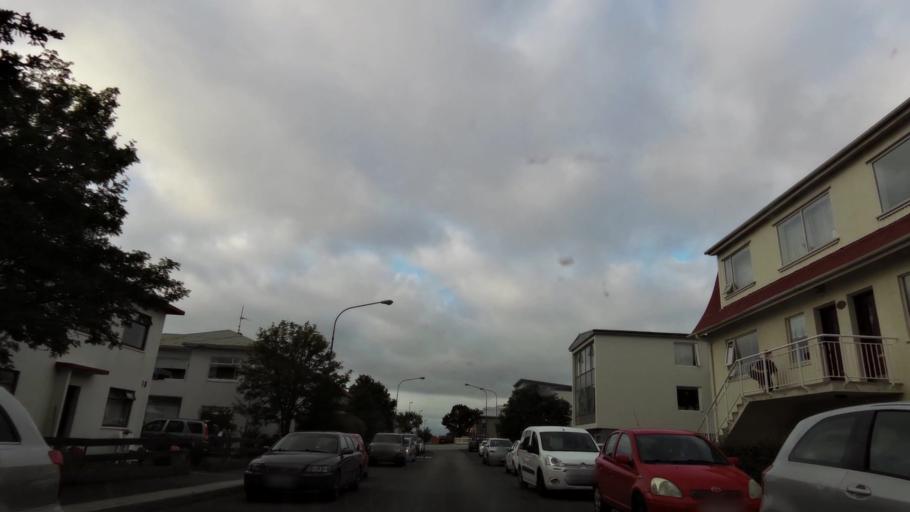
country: IS
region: Capital Region
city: Hafnarfjoerdur
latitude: 64.0633
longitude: -21.9483
